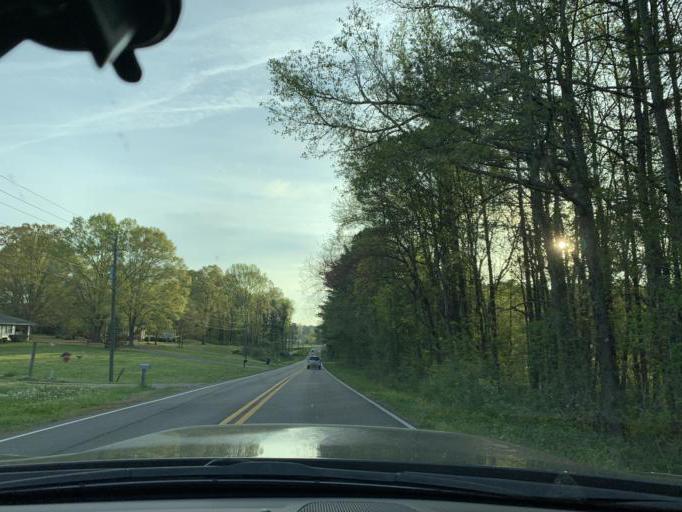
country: US
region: Georgia
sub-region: Forsyth County
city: Cumming
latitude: 34.2460
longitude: -84.1693
